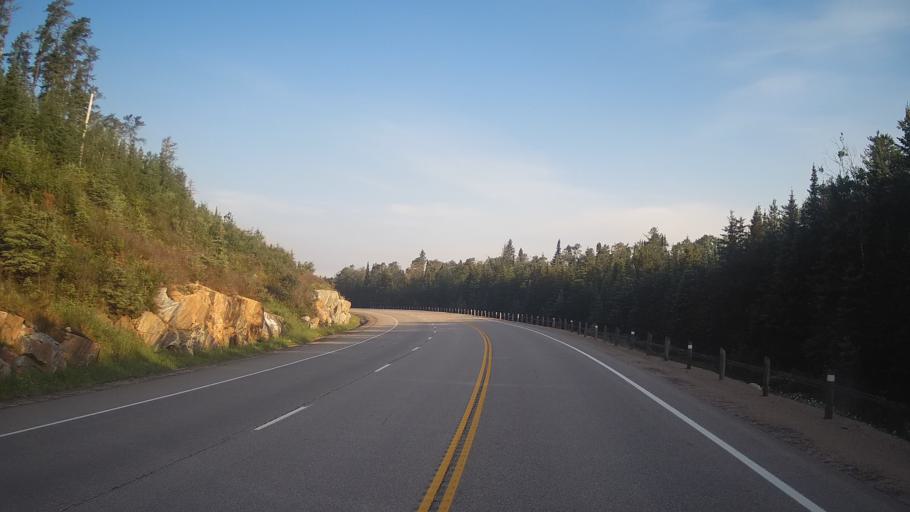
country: CA
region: Ontario
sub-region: Rainy River District
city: Atikokan
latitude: 49.3431
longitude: -91.4793
